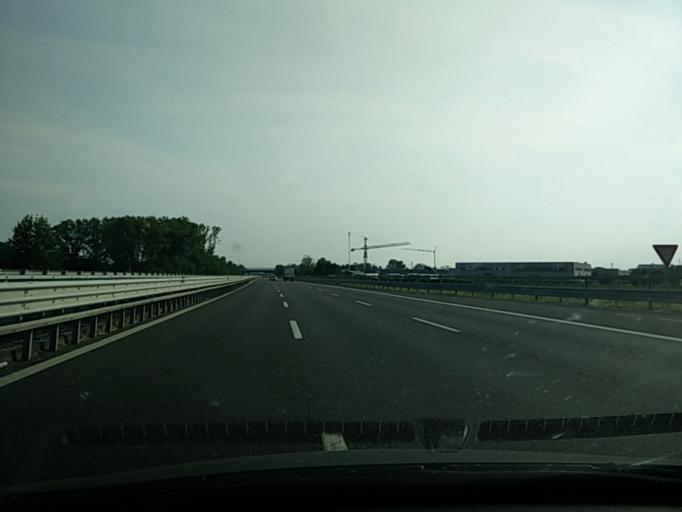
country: IT
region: Lombardy
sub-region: Citta metropolitana di Milano
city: Zibido San Giacomo
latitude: 45.3610
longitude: 9.1170
